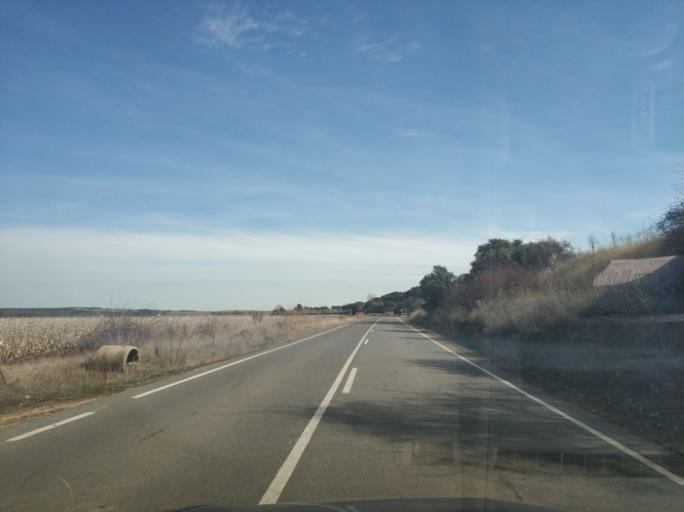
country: ES
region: Castille and Leon
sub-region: Provincia de Salamanca
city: Valverdon
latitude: 41.0371
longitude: -5.7776
